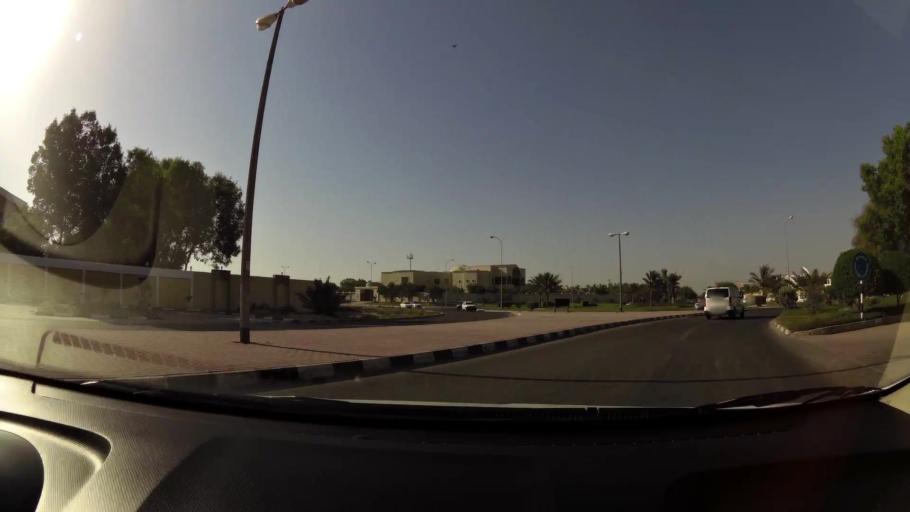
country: AE
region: Ajman
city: Ajman
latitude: 25.4047
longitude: 55.4721
